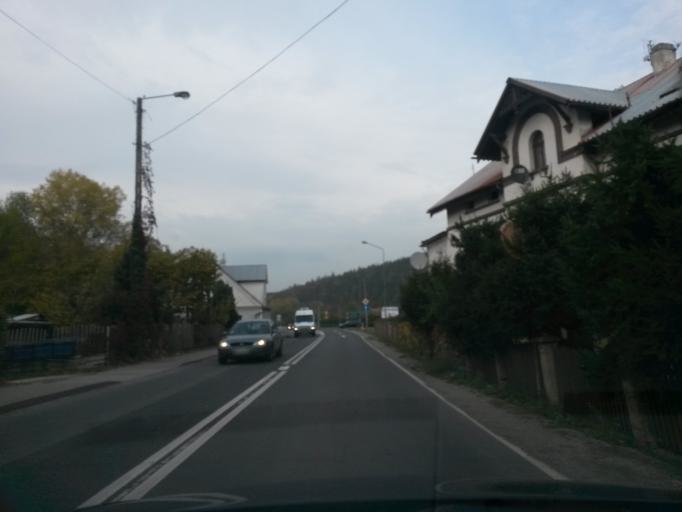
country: PL
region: Lower Silesian Voivodeship
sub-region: Powiat klodzki
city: Klodzko
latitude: 50.3720
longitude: 16.6744
